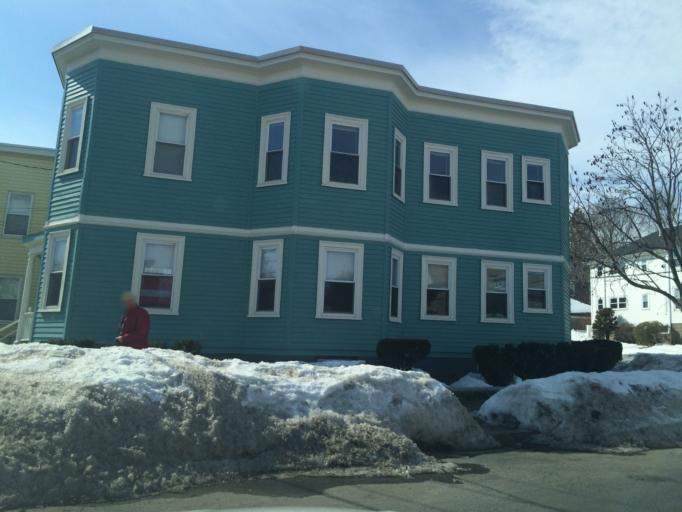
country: US
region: Massachusetts
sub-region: Middlesex County
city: Watertown
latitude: 42.3783
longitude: -71.1590
